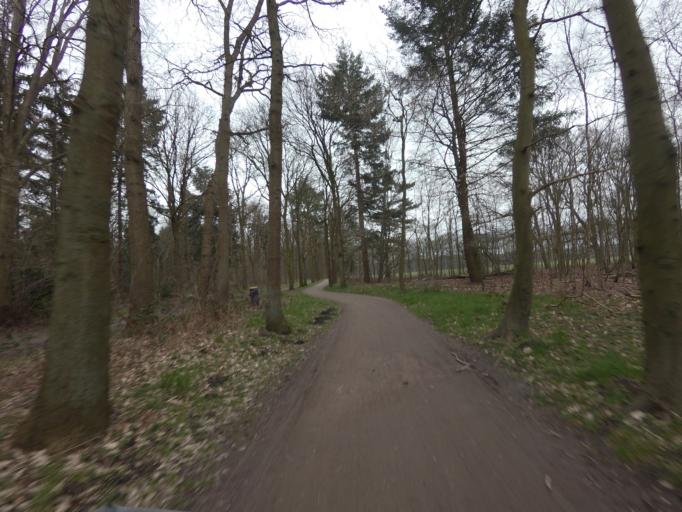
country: NL
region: North Holland
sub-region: Gemeente Hilversum
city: Hilversum
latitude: 52.2324
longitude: 5.1459
